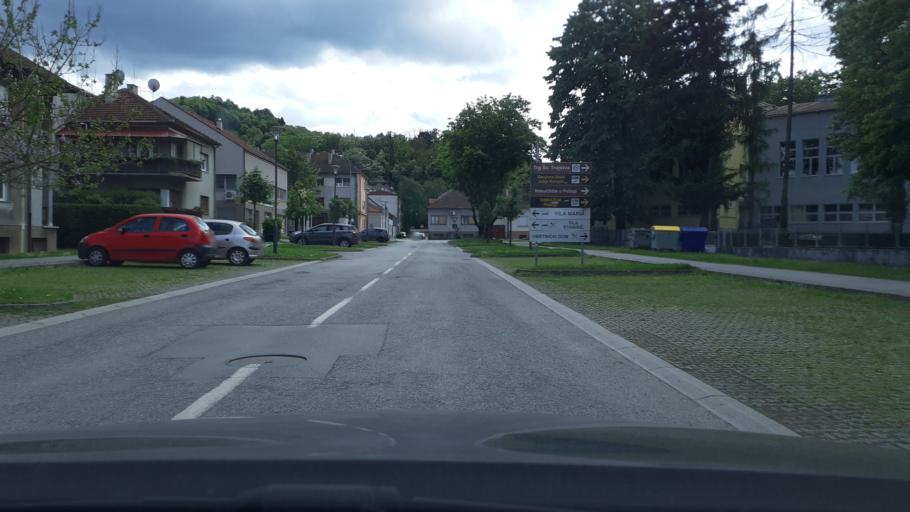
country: HR
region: Pozesko-Slavonska
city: Pozega
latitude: 45.3355
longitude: 17.6810
